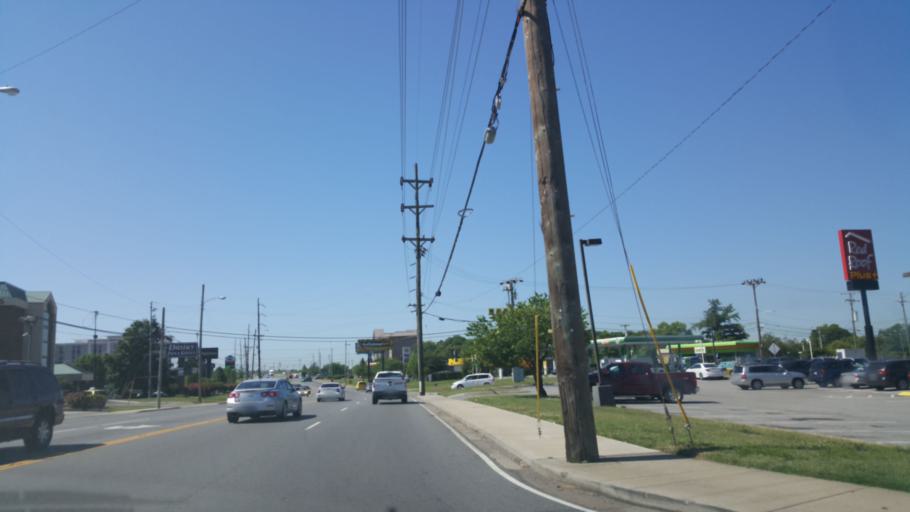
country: US
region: Tennessee
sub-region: Davidson County
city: Lakewood
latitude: 36.1459
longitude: -86.6667
